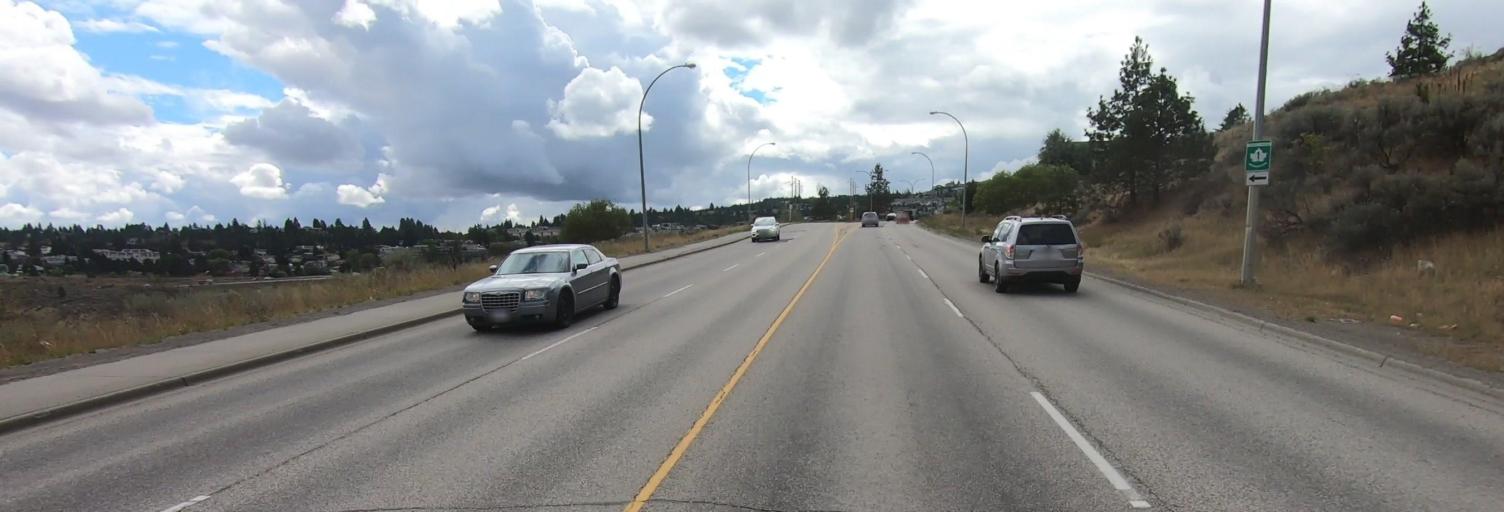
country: CA
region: British Columbia
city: Kamloops
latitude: 50.6600
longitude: -120.3698
